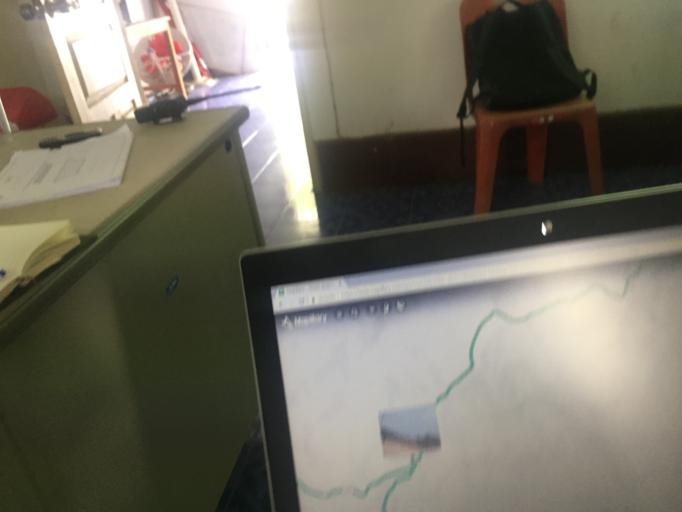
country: TH
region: Nan
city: Chaloem Phra Kiat
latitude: 19.8933
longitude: 101.1241
